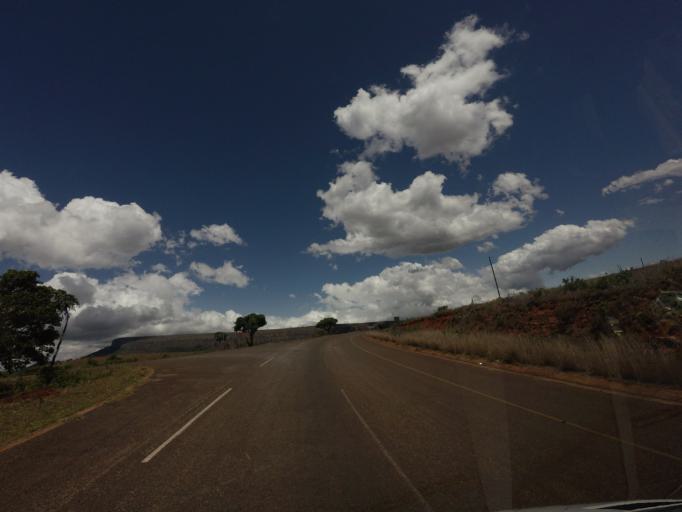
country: ZA
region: Limpopo
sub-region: Mopani District Municipality
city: Hoedspruit
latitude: -24.6076
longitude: 30.8137
